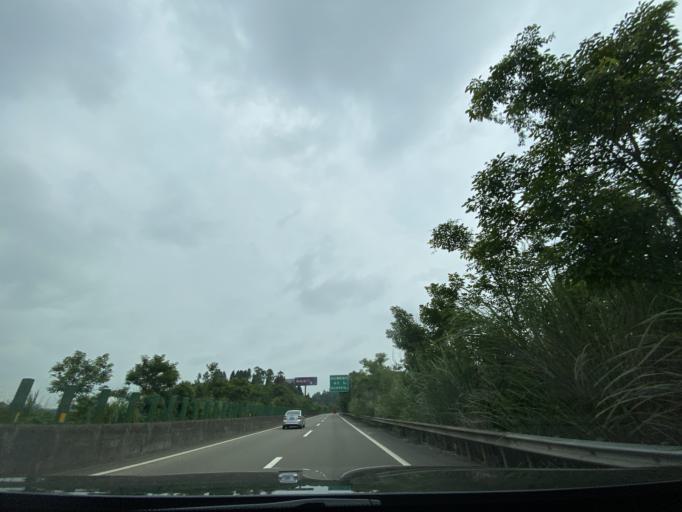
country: CN
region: Sichuan
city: Neijiang
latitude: 29.6622
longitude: 104.9802
